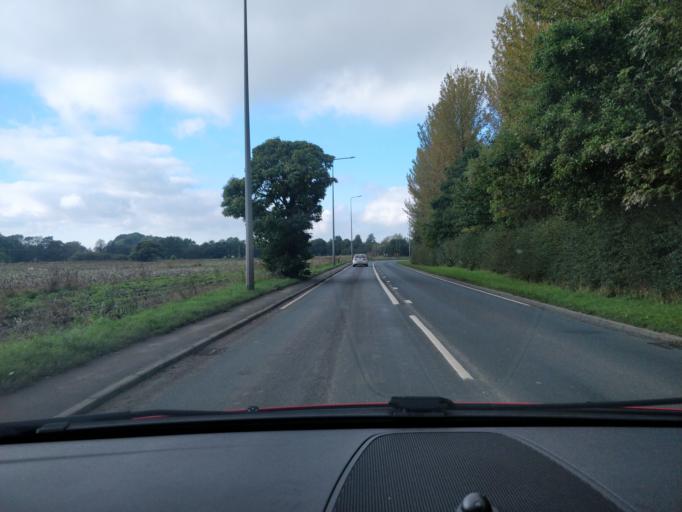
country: GB
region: England
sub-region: Lancashire
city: Ormskirk
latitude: 53.5862
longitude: -2.9124
